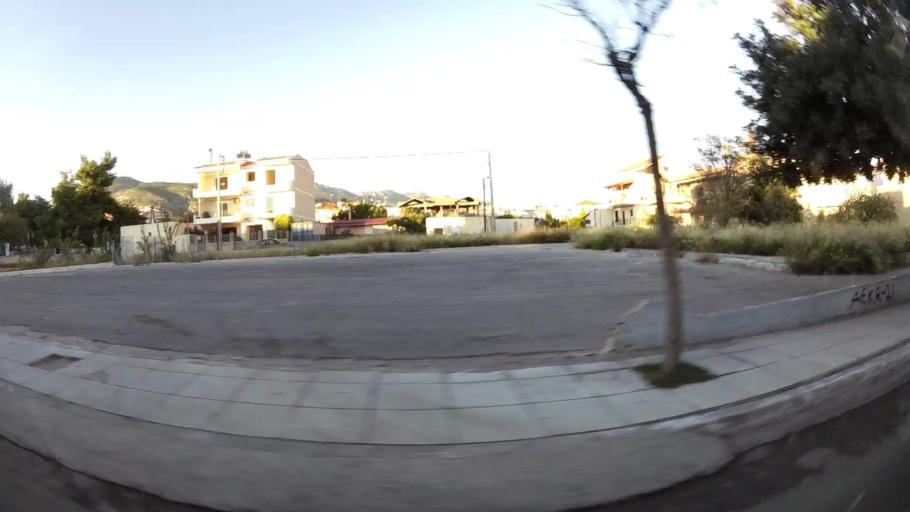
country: GR
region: Attica
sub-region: Nomarchia Dytikis Attikis
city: Ano Liosia
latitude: 38.0829
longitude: 23.7062
